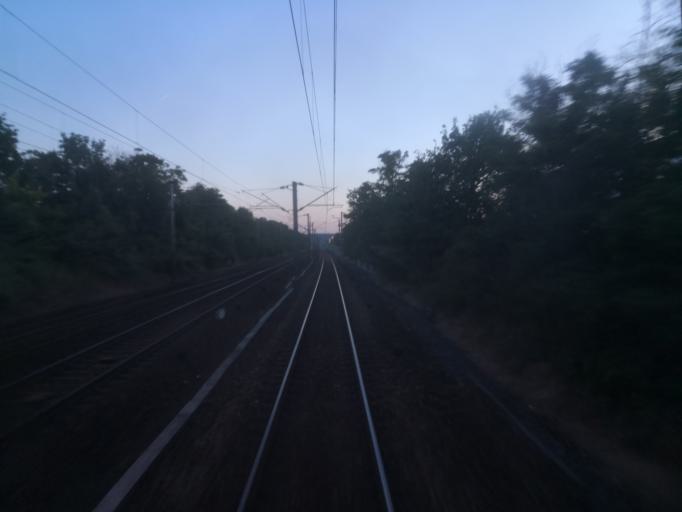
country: FR
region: Ile-de-France
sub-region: Departement des Yvelines
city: Aubergenville
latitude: 48.9747
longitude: 1.8564
